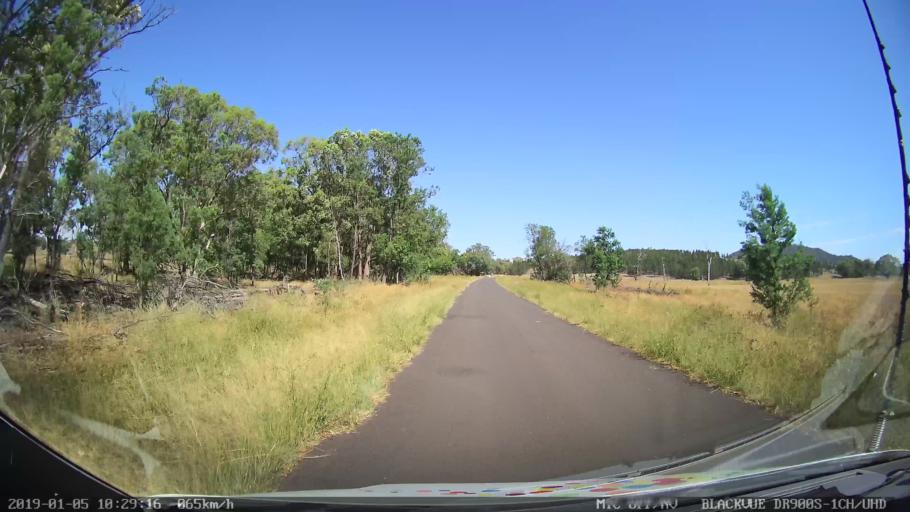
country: AU
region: New South Wales
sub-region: Gilgandra
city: Gilgandra
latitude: -31.5409
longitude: 148.9317
